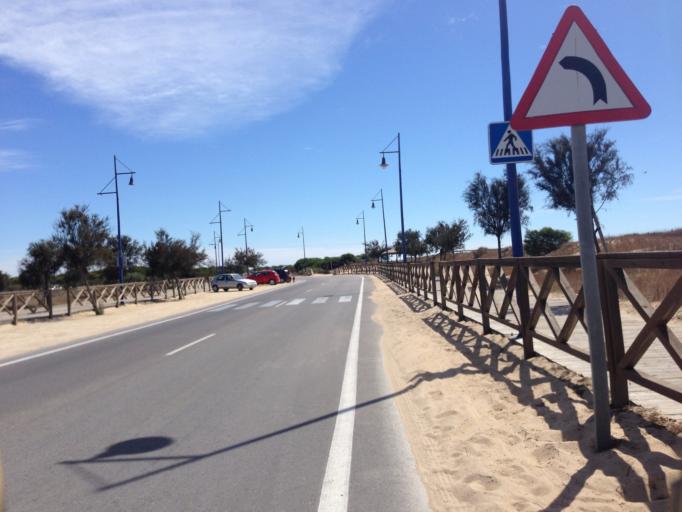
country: ES
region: Andalusia
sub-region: Provincia de Cadiz
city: Chiclana de la Frontera
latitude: 36.3878
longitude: -6.2070
